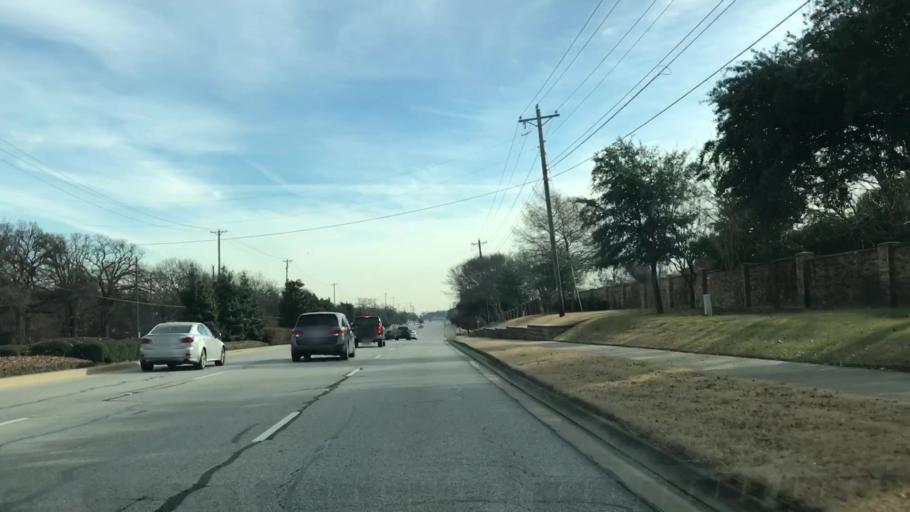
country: US
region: Texas
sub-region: Tarrant County
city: Southlake
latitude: 32.9413
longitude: -97.1697
